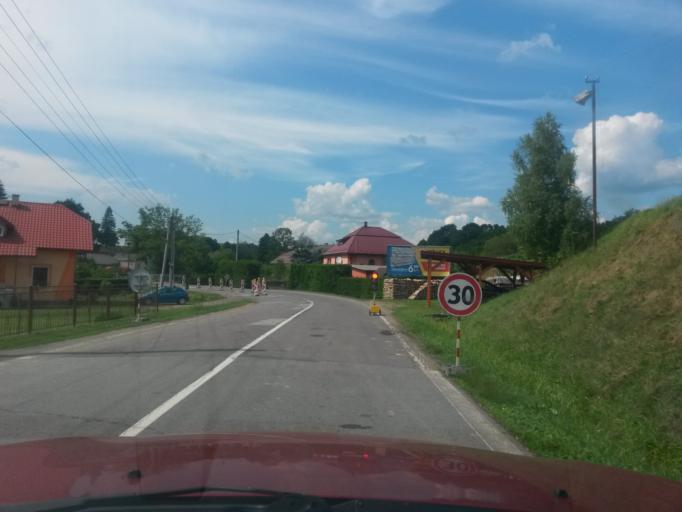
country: UA
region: Zakarpattia
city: Velykyi Bereznyi
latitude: 48.9023
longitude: 22.3858
